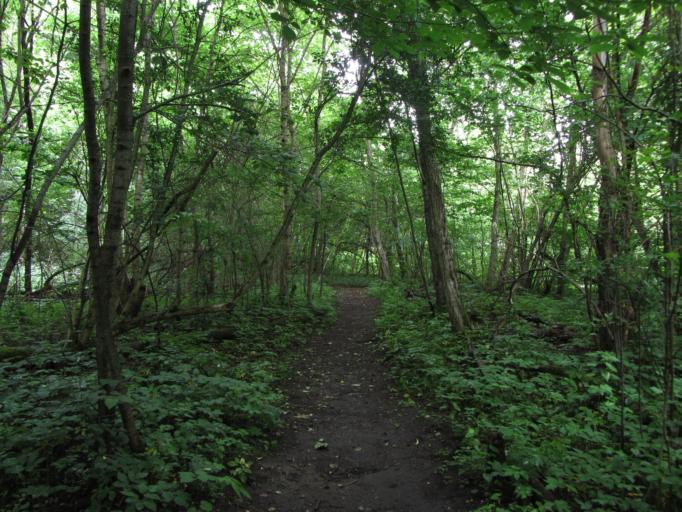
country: LT
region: Vilnius County
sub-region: Vilniaus Rajonas
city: Vievis
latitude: 54.8201
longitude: 24.9327
